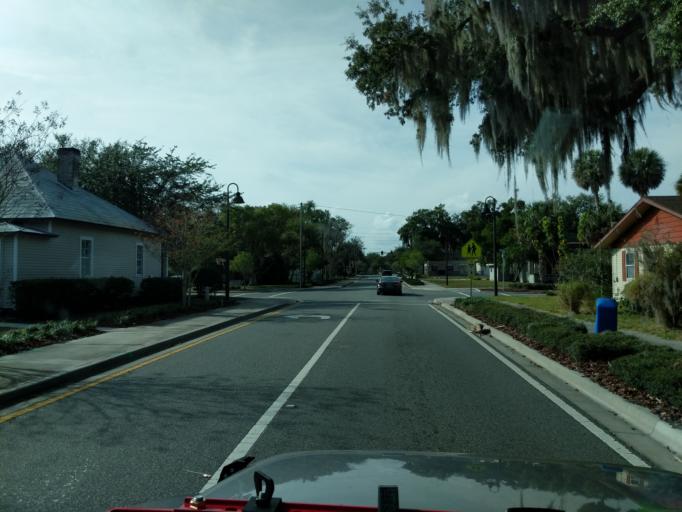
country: US
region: Florida
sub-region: Lake County
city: Tavares
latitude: 28.8052
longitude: -81.7297
